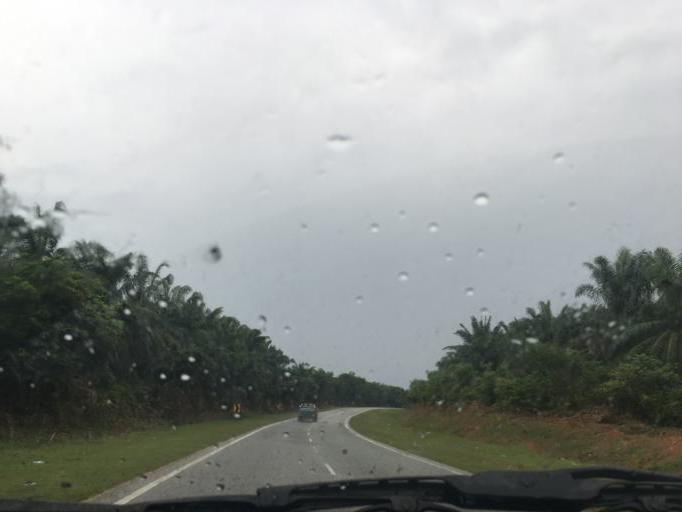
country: MY
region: Kedah
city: Sungai Petani
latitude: 5.6228
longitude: 100.6376
